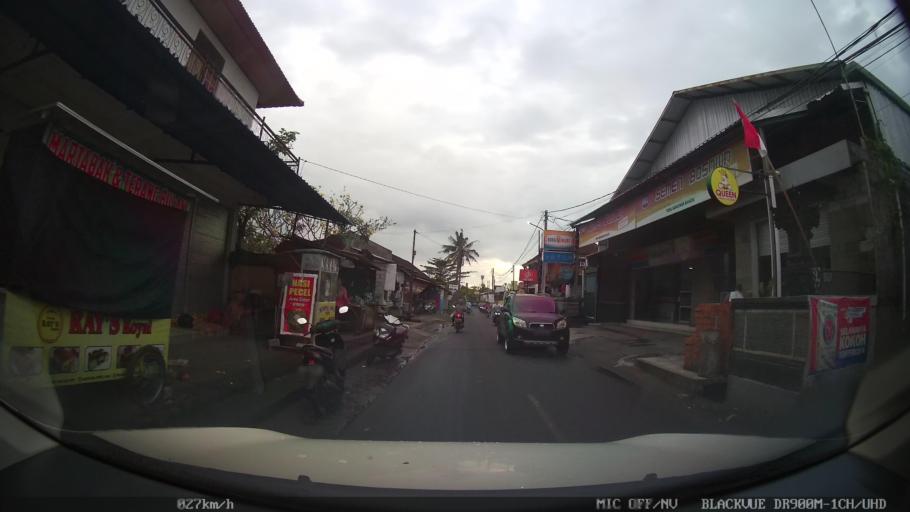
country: ID
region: Bali
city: Banjar Paangkelod
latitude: -8.6189
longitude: 115.2584
